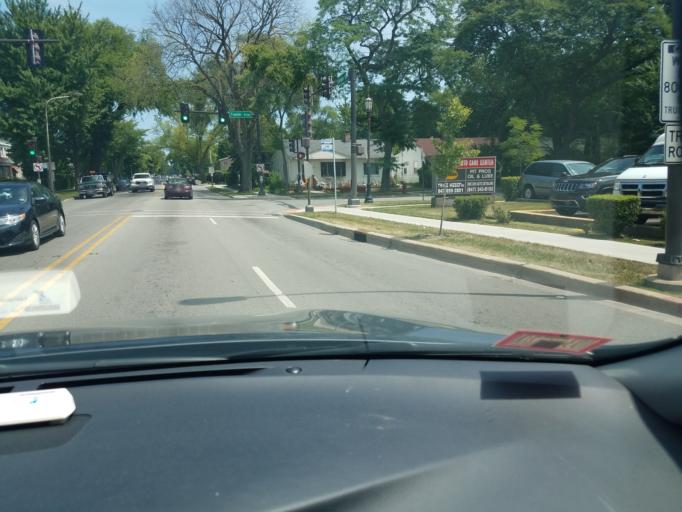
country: US
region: Illinois
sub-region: Cook County
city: Evanston
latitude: 42.0410
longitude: -87.7073
